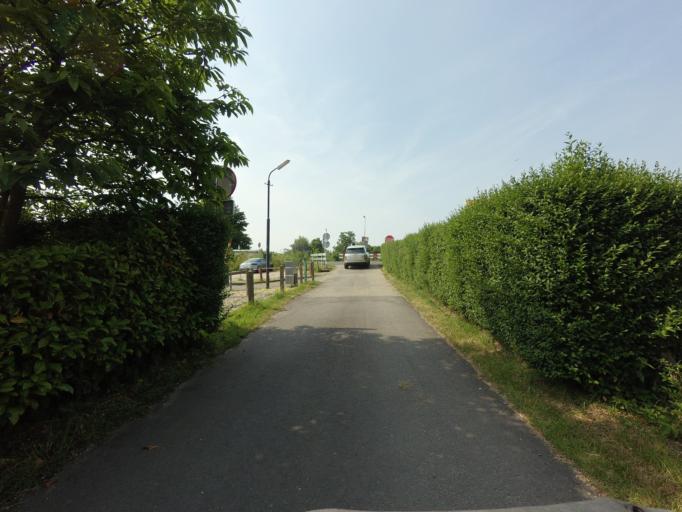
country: NL
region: Utrecht
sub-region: Stichtse Vecht
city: Maarssen
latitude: 52.1654
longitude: 5.0467
